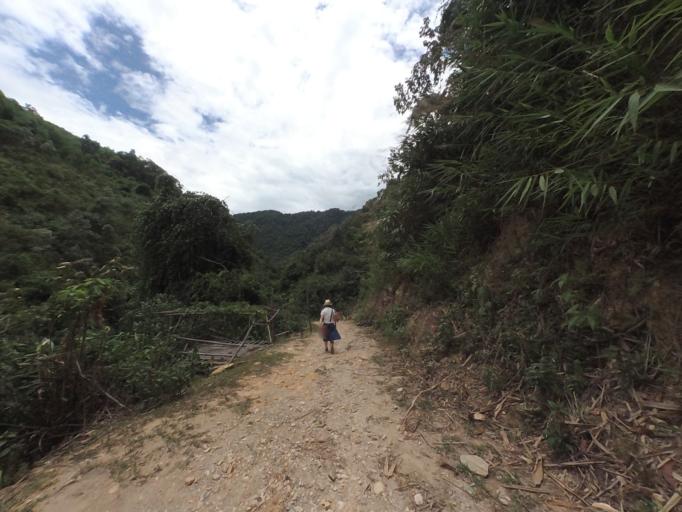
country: VN
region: Thua Thien-Hue
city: A Luoi
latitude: 16.3044
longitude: 107.3250
